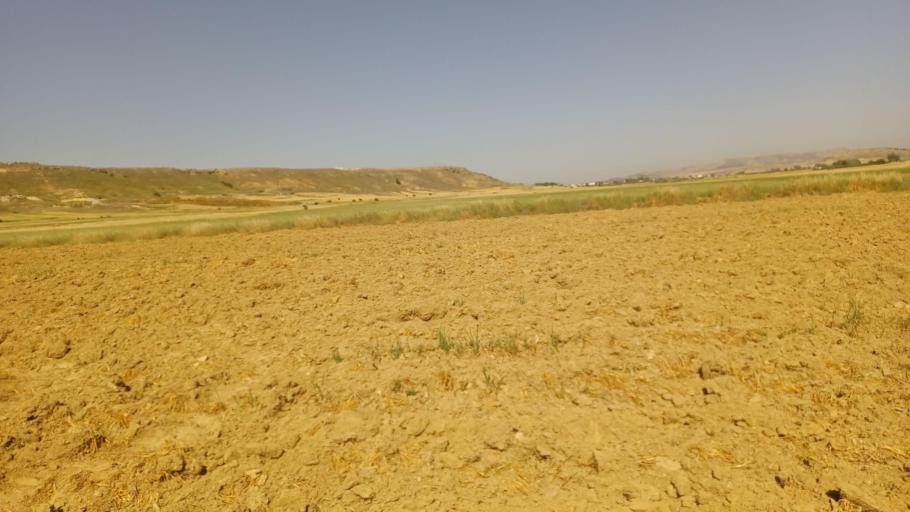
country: CY
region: Lefkosia
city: Mammari
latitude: 35.1720
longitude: 33.2309
